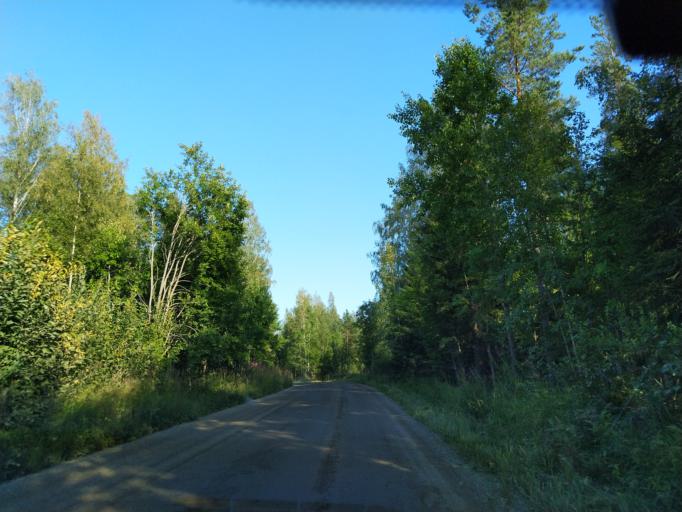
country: FI
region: Central Finland
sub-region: Jaemsae
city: Kuhmoinen
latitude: 61.6035
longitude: 25.1450
